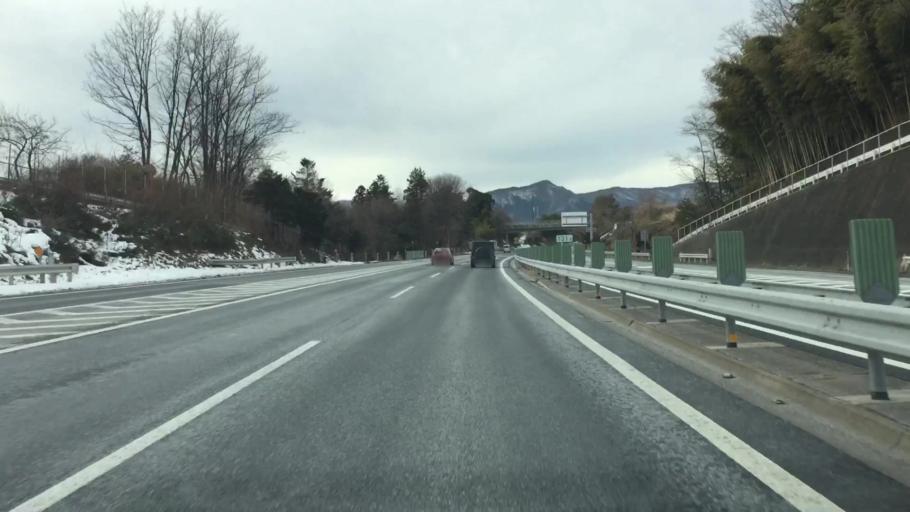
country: JP
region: Gunma
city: Numata
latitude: 36.6768
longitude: 139.0164
